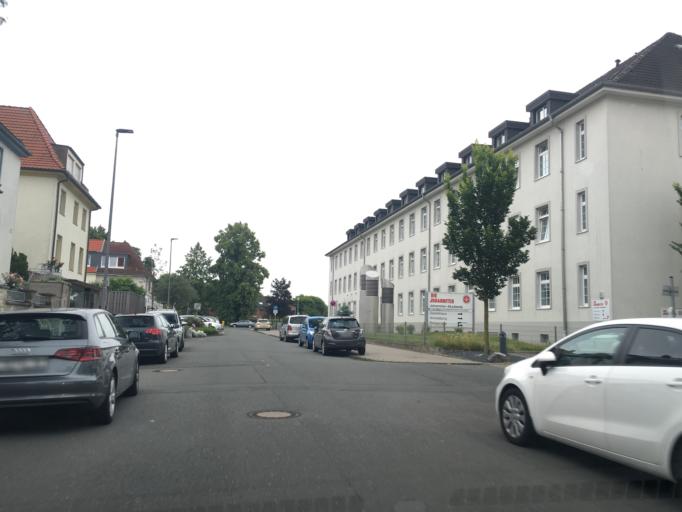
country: DE
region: North Rhine-Westphalia
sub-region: Regierungsbezirk Munster
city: Muenster
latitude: 51.9414
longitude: 7.6201
